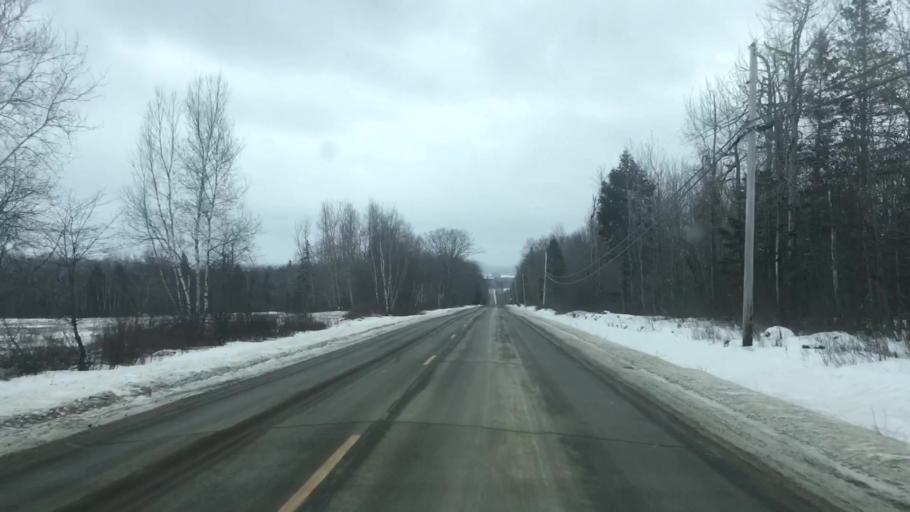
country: US
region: Maine
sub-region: Washington County
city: East Machias
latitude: 44.9781
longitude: -67.4524
